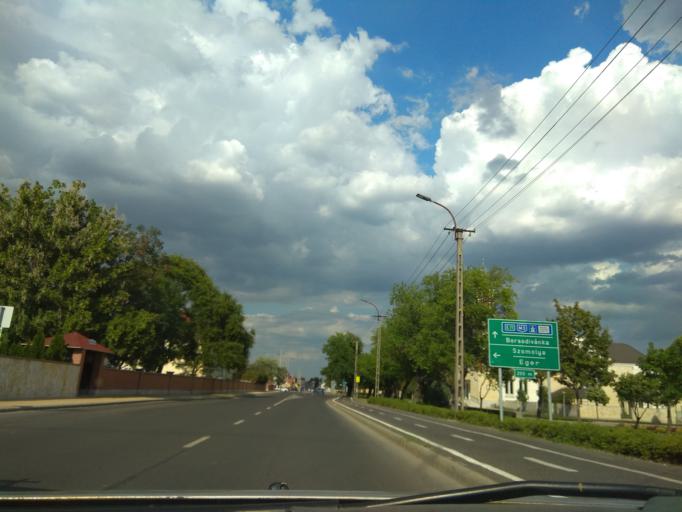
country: HU
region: Borsod-Abauj-Zemplen
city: Mezokovesd
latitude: 47.8051
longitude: 20.5609
